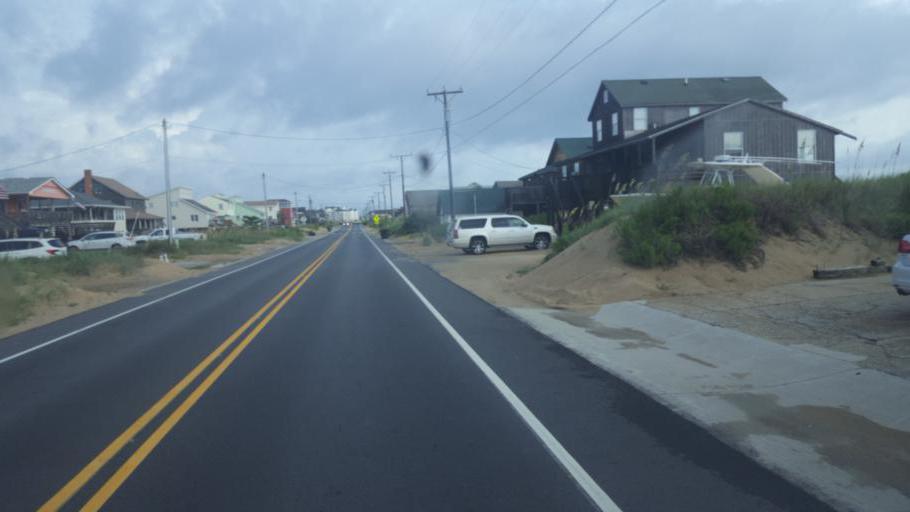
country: US
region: North Carolina
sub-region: Dare County
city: Kitty Hawk
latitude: 36.0928
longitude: -75.7067
